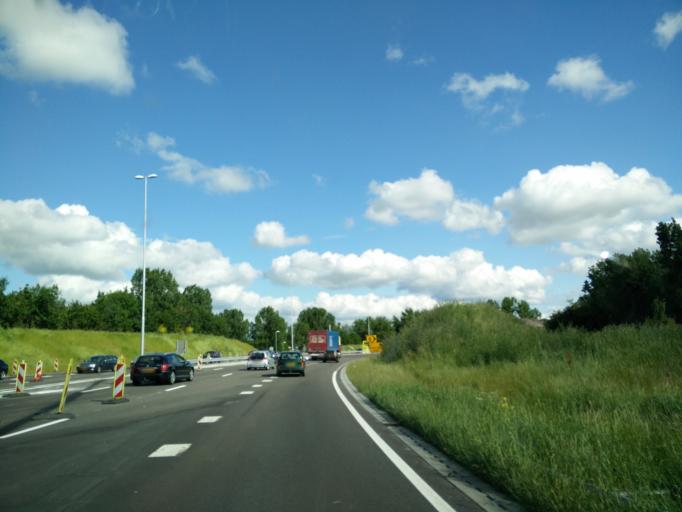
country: NL
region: Groningen
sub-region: Gemeente Groningen
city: Korrewegwijk
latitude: 53.2477
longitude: 6.5794
